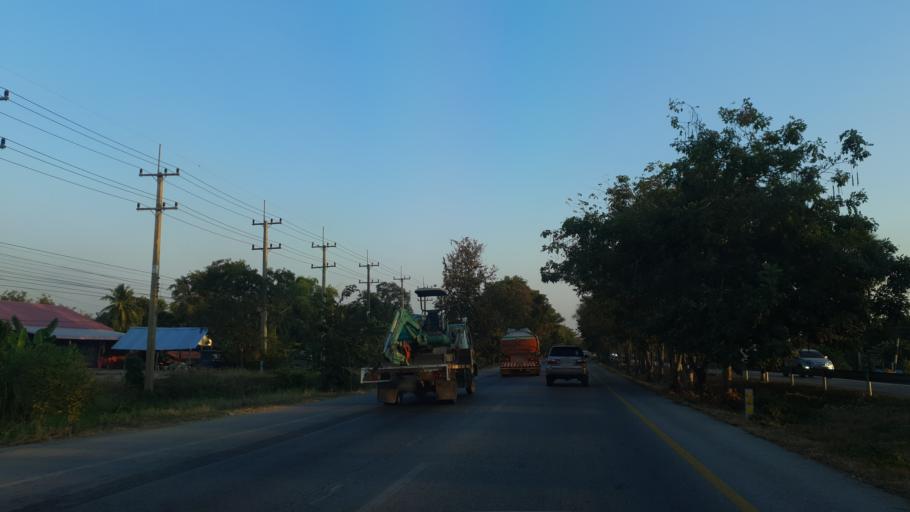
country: TH
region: Nakhon Sawan
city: Banphot Phisai
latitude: 15.9069
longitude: 99.8904
